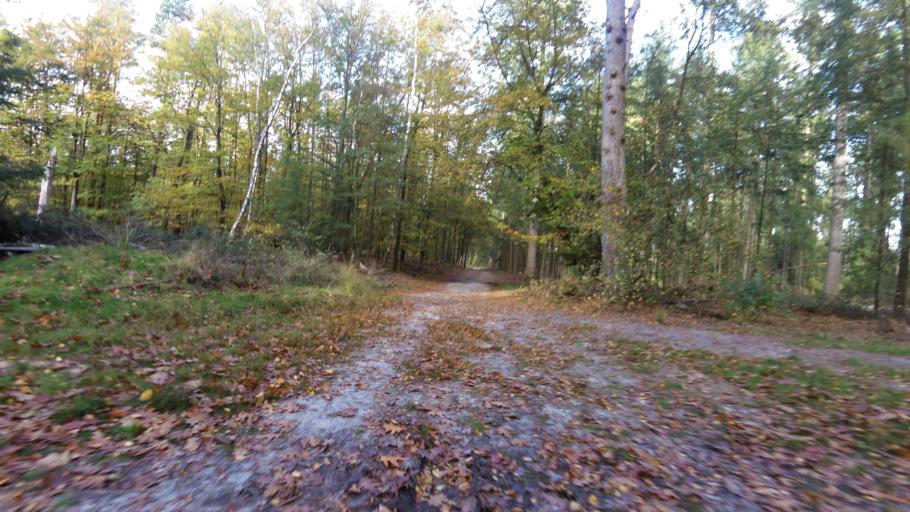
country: NL
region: Gelderland
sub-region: Gemeente Heerde
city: Heerde
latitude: 52.4186
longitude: 6.0367
